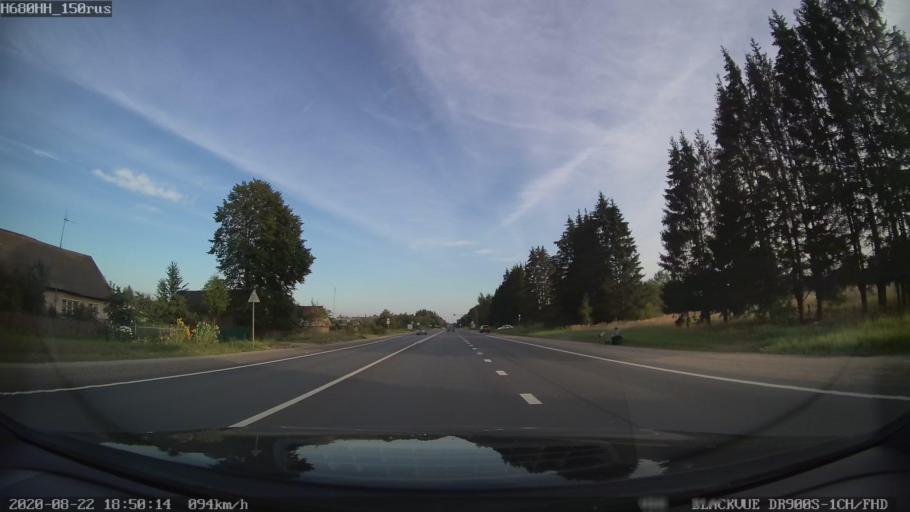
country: RU
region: Tverskaya
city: Rameshki
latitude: 57.2689
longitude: 36.0723
